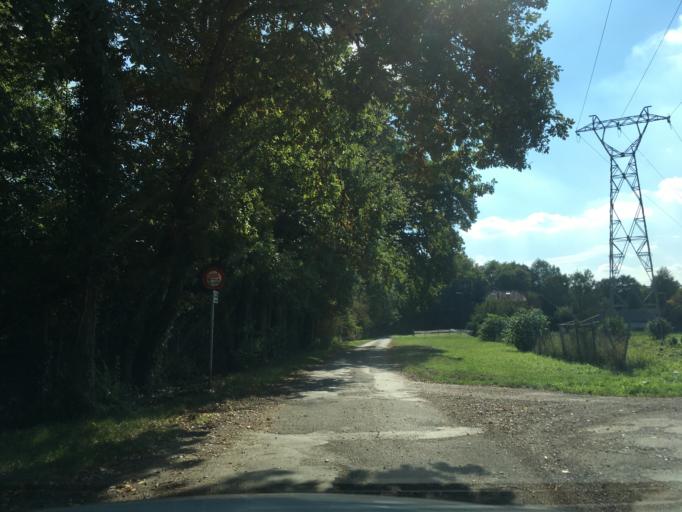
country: FR
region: Alsace
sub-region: Departement du Haut-Rhin
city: Colmar
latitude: 48.0585
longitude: 7.3710
